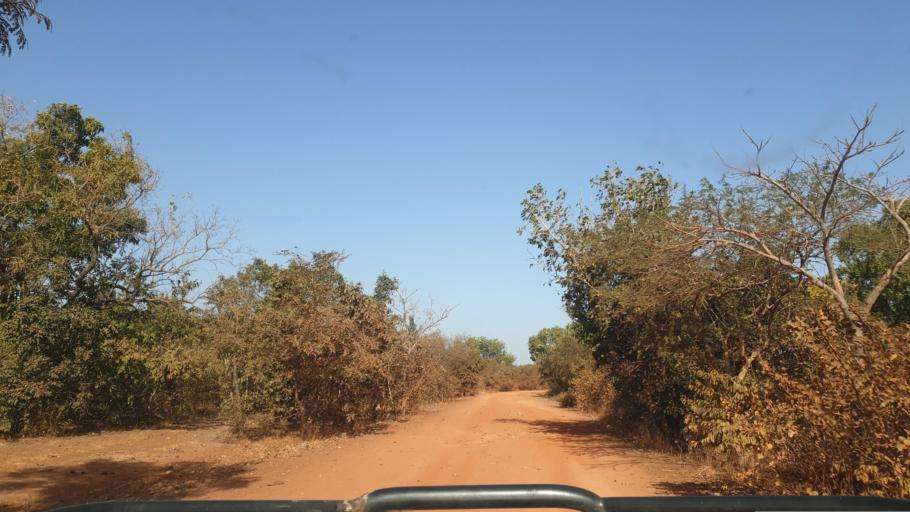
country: ML
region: Sikasso
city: Bougouni
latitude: 11.7759
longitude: -6.9058
